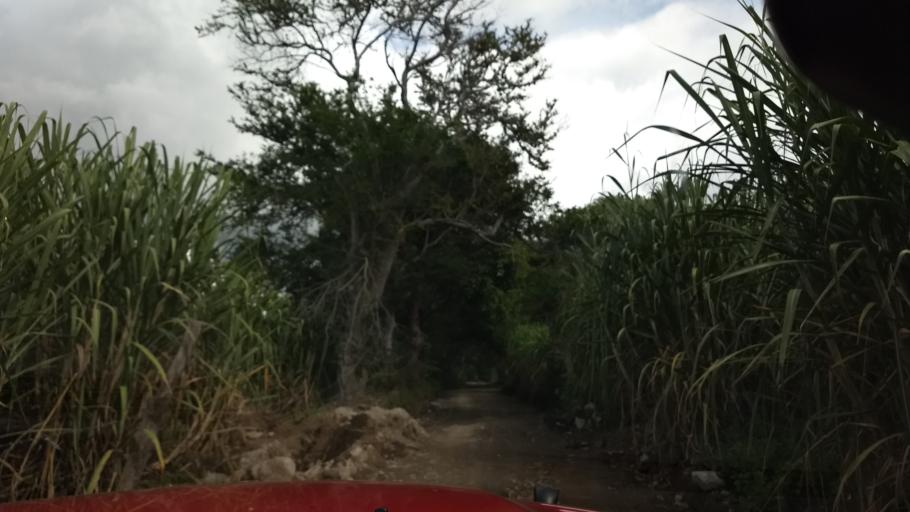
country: MX
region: Colima
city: Suchitlan
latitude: 19.4618
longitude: -103.7551
